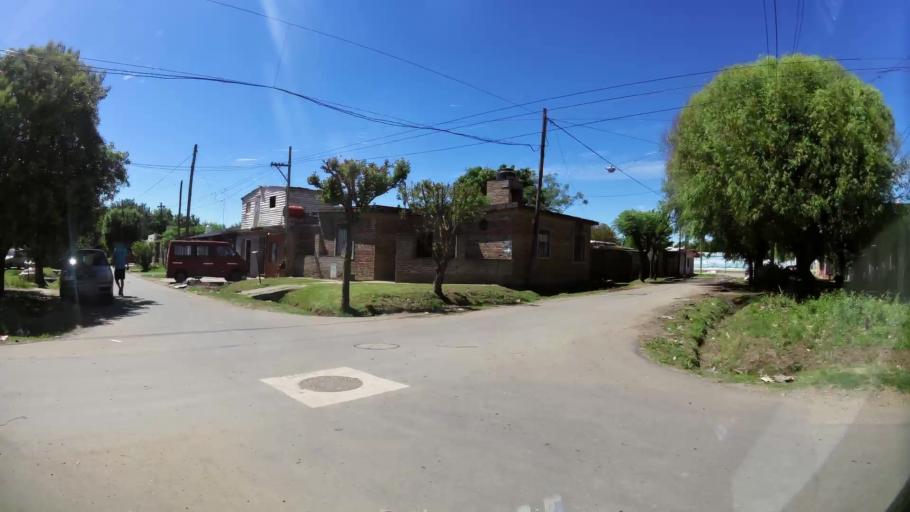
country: AR
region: Santa Fe
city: Perez
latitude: -32.9588
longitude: -60.7152
